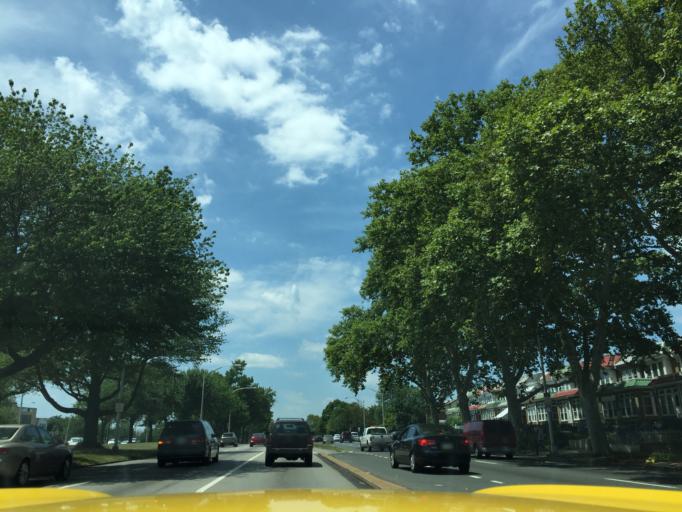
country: US
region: Pennsylvania
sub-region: Montgomery County
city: Rockledge
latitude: 40.0267
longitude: -75.1177
